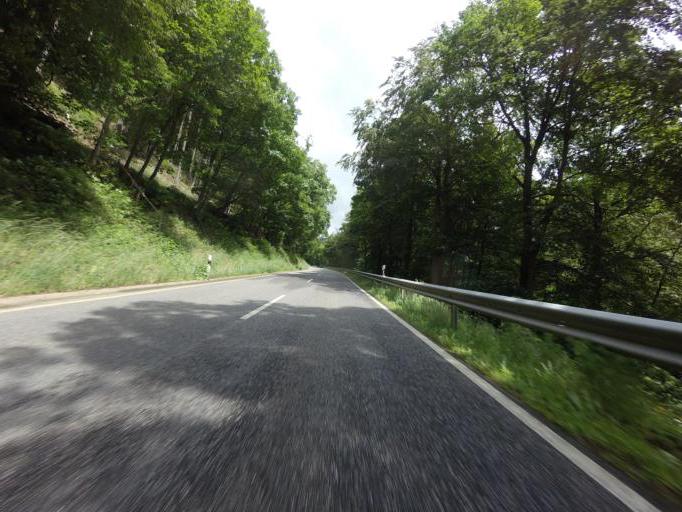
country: DE
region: Rheinland-Pfalz
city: Kaltenborn
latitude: 50.3878
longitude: 6.9887
